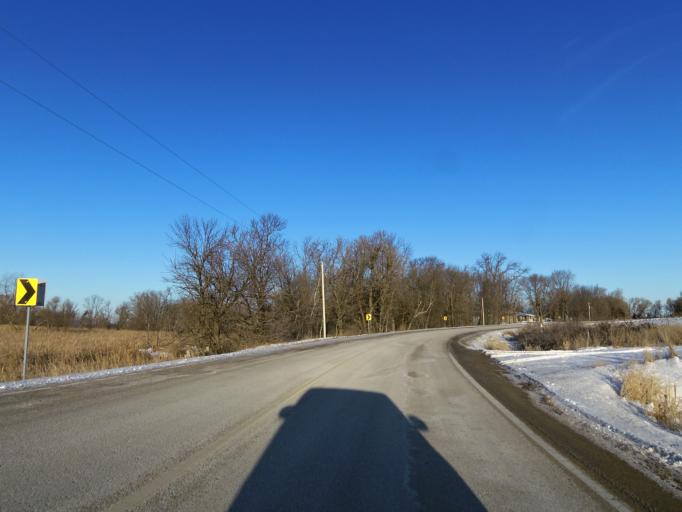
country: US
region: Minnesota
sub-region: Scott County
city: Jordan
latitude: 44.6594
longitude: -93.5308
